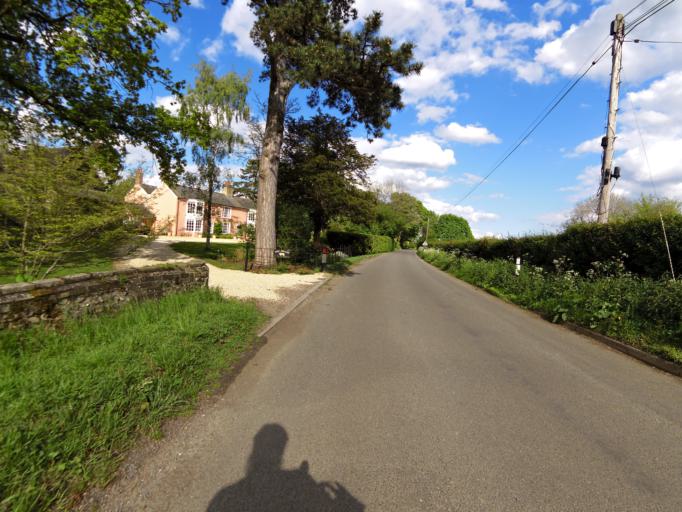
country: GB
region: England
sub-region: Suffolk
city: Woolpit
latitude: 52.2224
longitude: 0.8541
